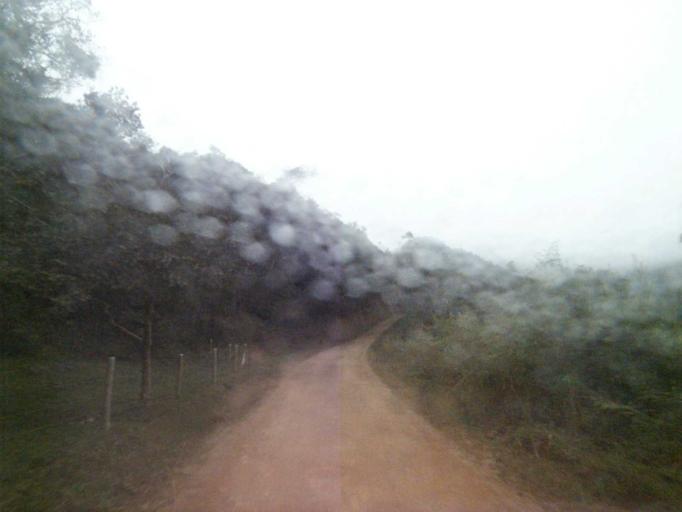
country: BR
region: Santa Catarina
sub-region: Anitapolis
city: Anitapolis
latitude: -27.8807
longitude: -49.1323
